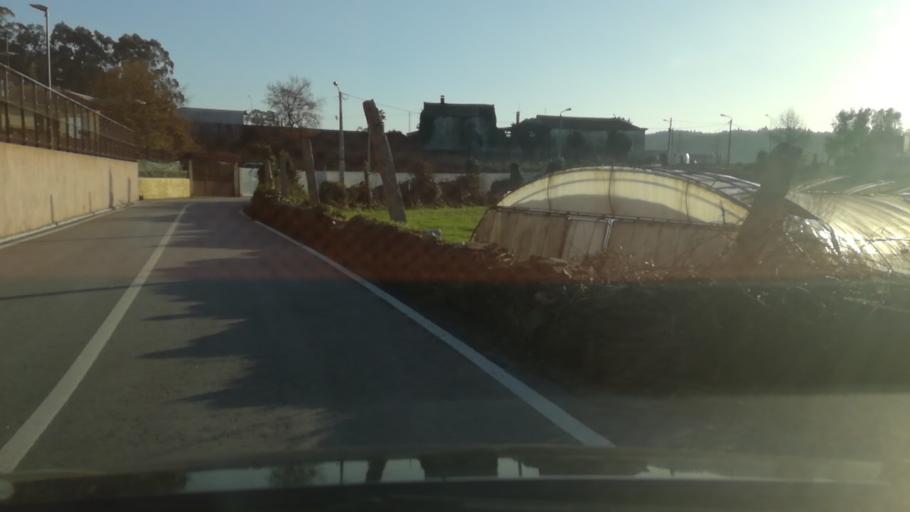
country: PT
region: Porto
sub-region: Trofa
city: Bougado
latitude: 41.3370
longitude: -8.5298
